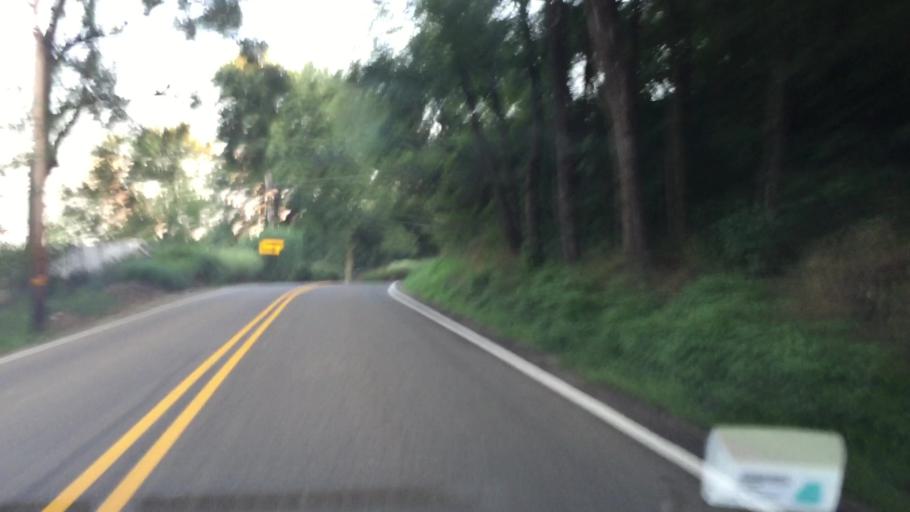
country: US
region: Pennsylvania
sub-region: Butler County
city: Evans City
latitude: 40.7376
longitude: -80.0714
